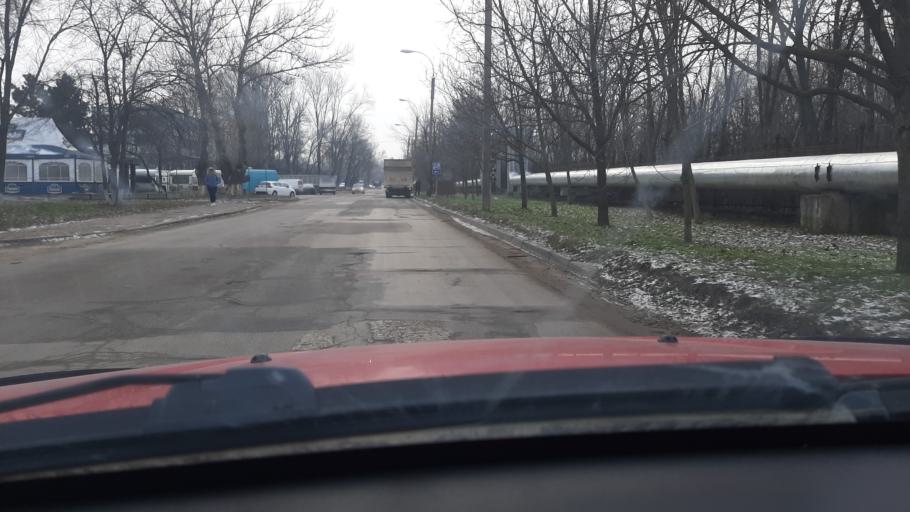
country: MD
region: Chisinau
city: Chisinau
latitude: 46.9761
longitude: 28.8933
